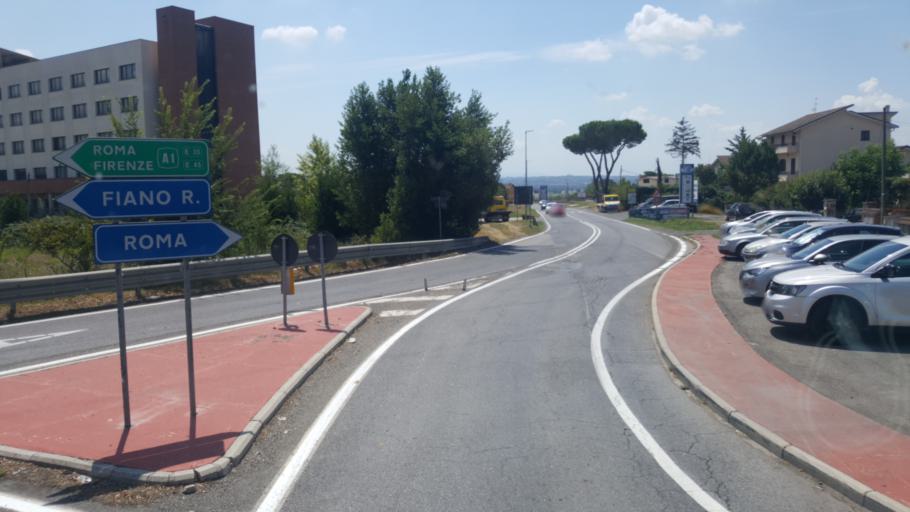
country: IT
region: Latium
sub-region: Citta metropolitana di Roma Capitale
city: Bivio di Capanelle
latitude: 42.1364
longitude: 12.5975
